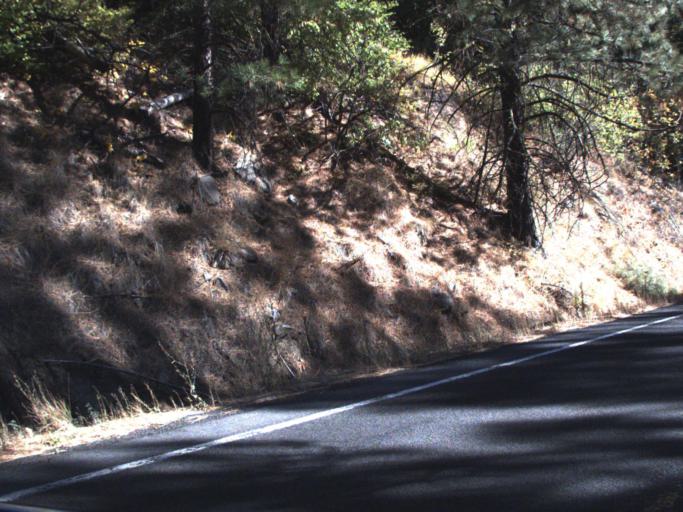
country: US
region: Washington
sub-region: Yakima County
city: Tieton
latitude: 46.6770
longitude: -121.0686
